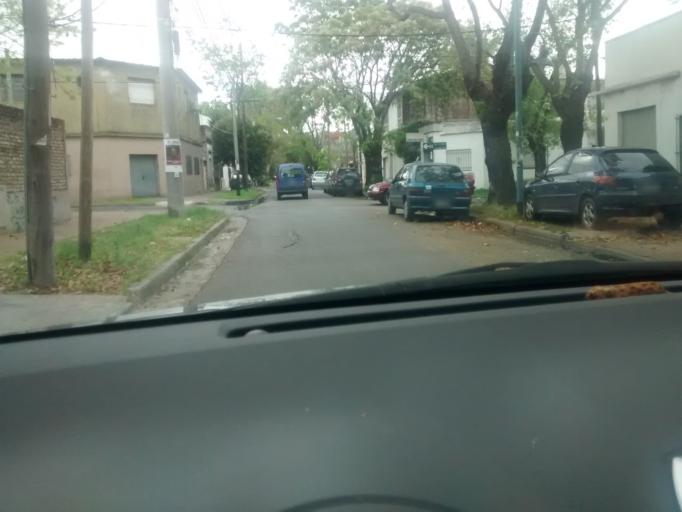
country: AR
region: Buenos Aires
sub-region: Partido de Vicente Lopez
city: Olivos
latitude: -34.5328
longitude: -58.5160
